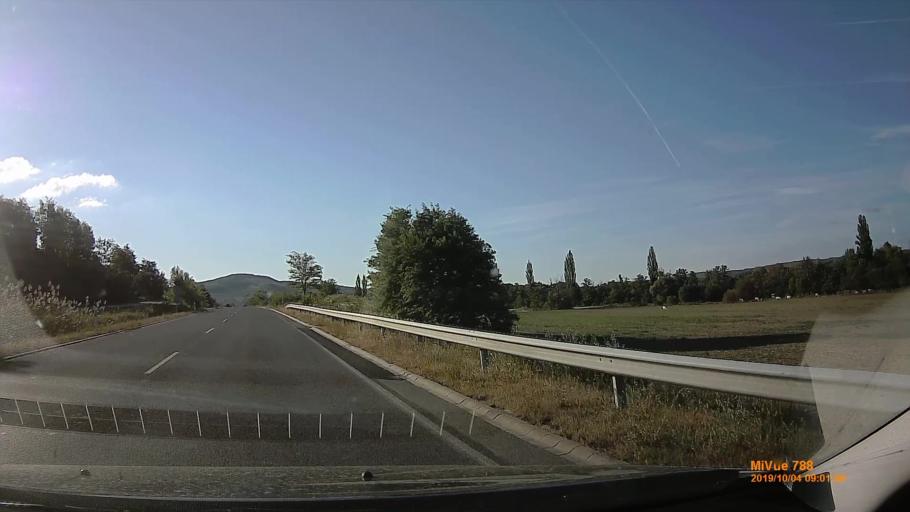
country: HU
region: Somogy
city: Karad
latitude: 46.7408
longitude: 17.7734
